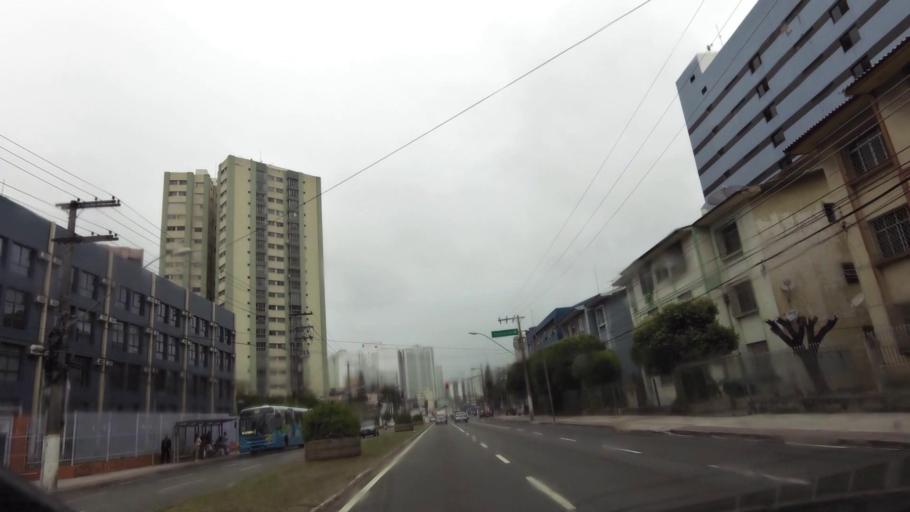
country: BR
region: Espirito Santo
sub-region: Vila Velha
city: Vila Velha
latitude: -20.3112
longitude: -40.3011
